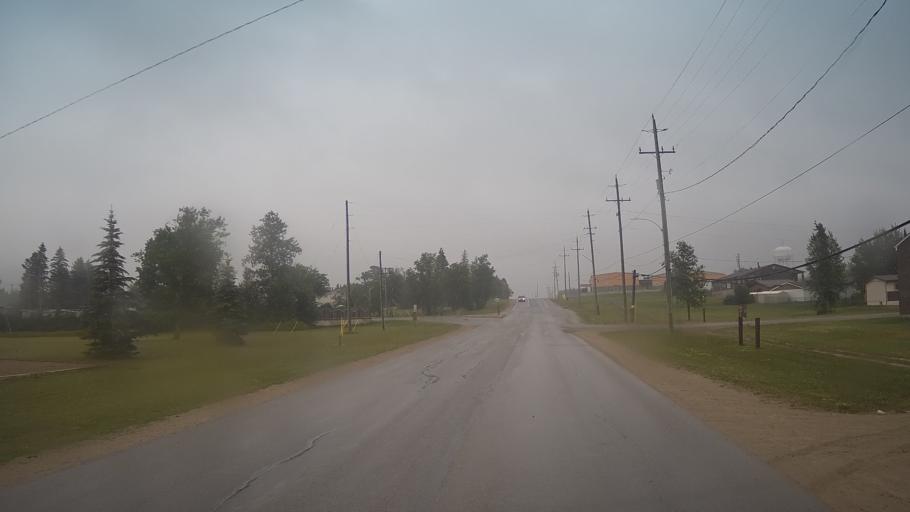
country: CA
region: Ontario
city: Greenstone
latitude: 49.7752
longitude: -86.5373
